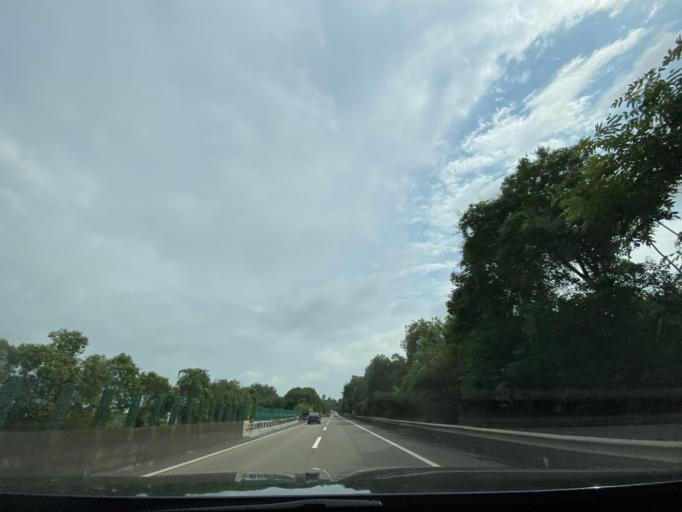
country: CN
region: Sichuan
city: Chonglong
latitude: 29.7091
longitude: 104.9409
